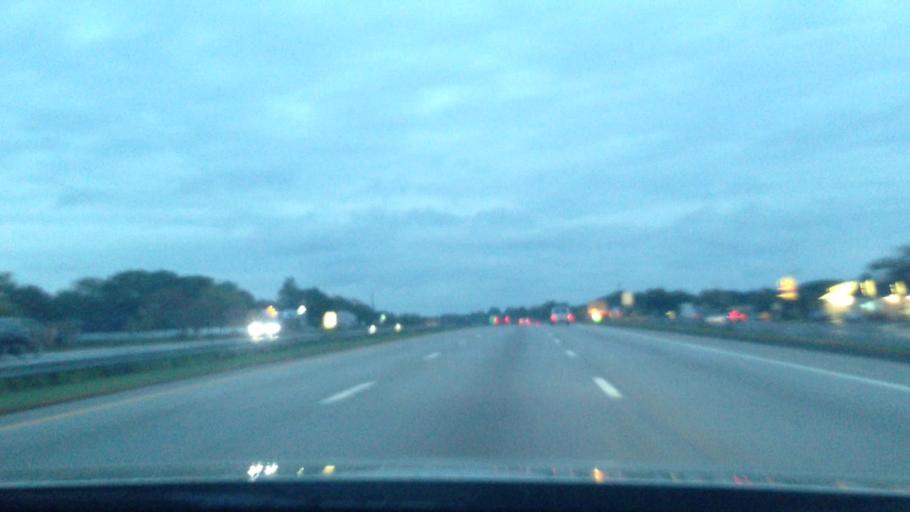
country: US
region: New York
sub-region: Suffolk County
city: Bohemia
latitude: 40.7530
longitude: -73.1207
